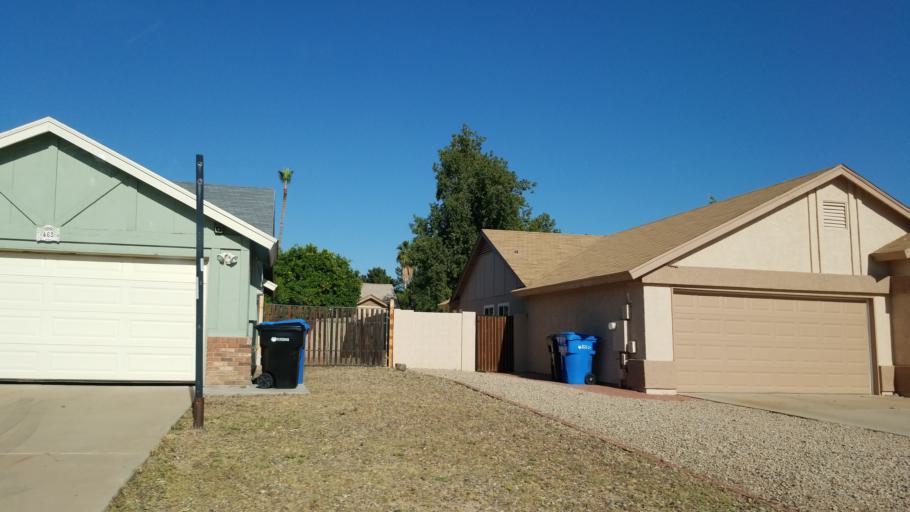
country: US
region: Arizona
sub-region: Maricopa County
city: Paradise Valley
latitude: 33.6204
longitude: -112.0003
